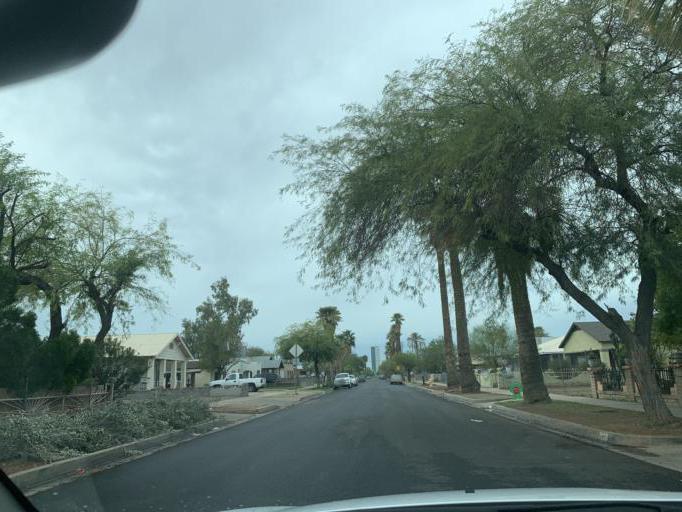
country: US
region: Arizona
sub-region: Maricopa County
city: Phoenix
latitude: 33.4558
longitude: -112.0503
